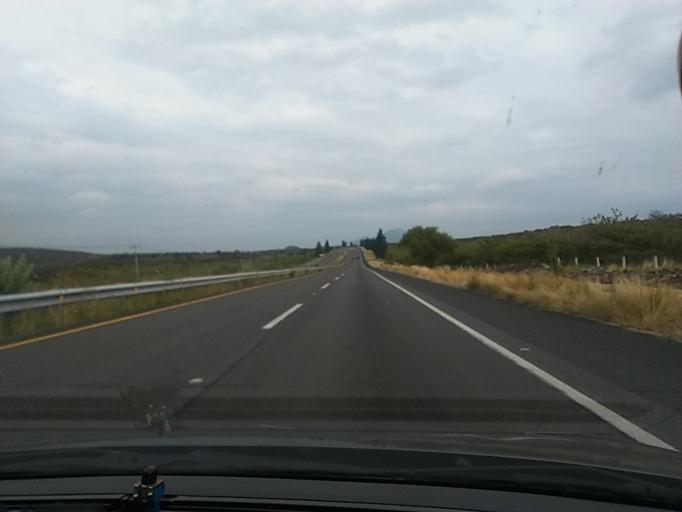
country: MX
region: Michoacan
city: Ecuandureo
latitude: 20.1702
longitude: -102.1471
